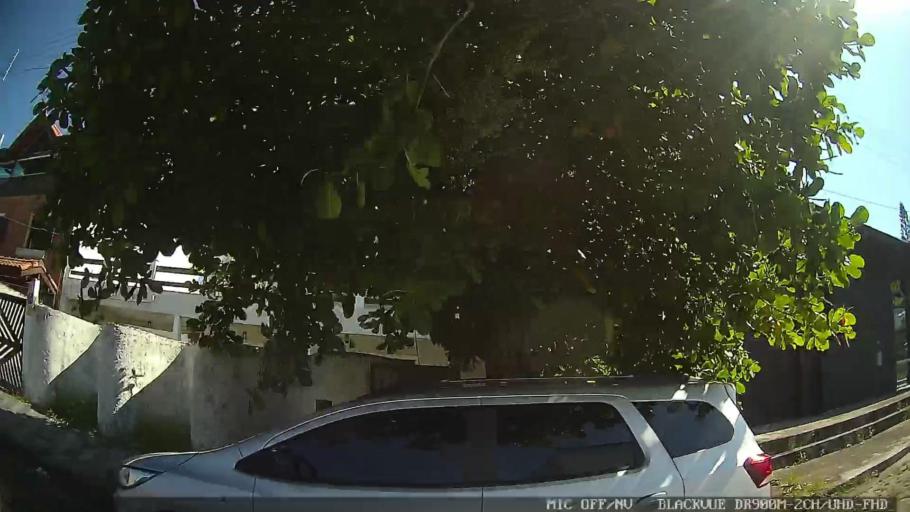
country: BR
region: Sao Paulo
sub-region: Peruibe
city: Peruibe
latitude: -24.2935
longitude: -46.9648
